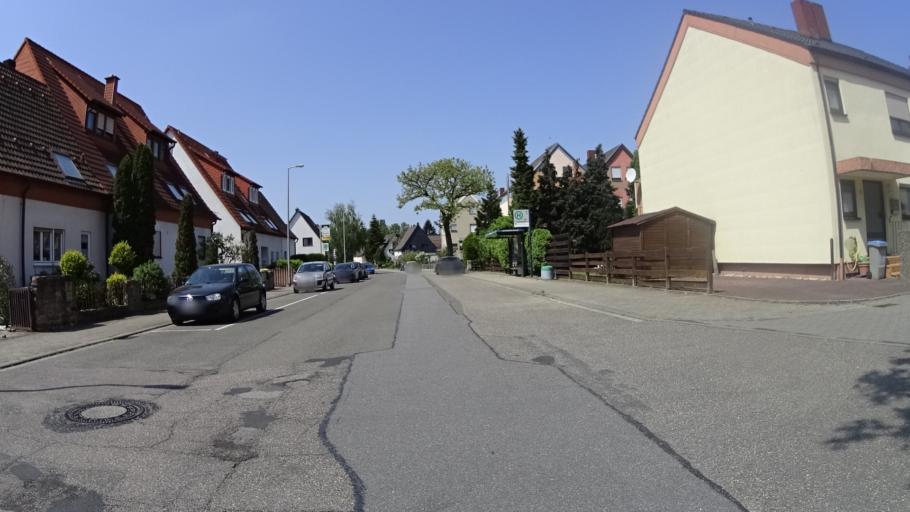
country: DE
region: Baden-Wuerttemberg
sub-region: Karlsruhe Region
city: Bruhl
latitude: 49.4200
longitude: 8.5288
